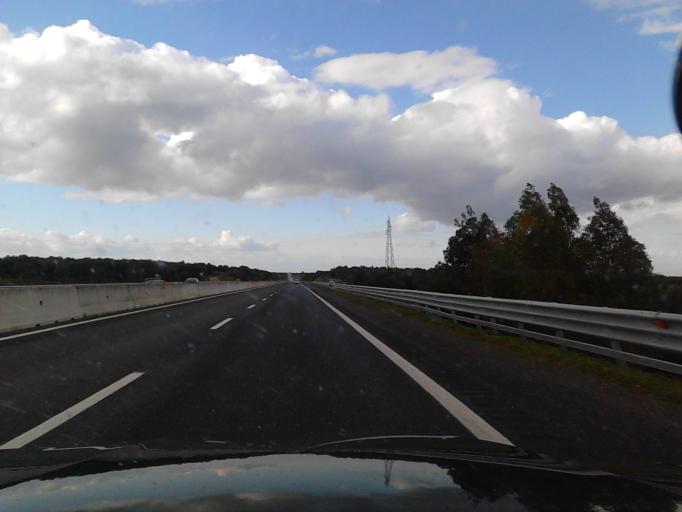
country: IT
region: Apulia
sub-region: Provincia di Barletta - Andria - Trani
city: Andria
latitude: 41.2584
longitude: 16.2728
